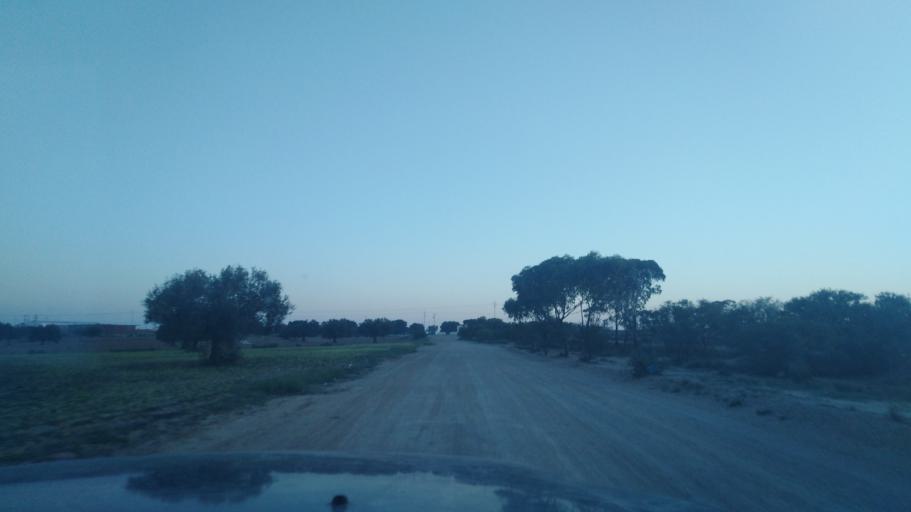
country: TN
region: Safaqis
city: Sfax
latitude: 34.7270
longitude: 10.4467
